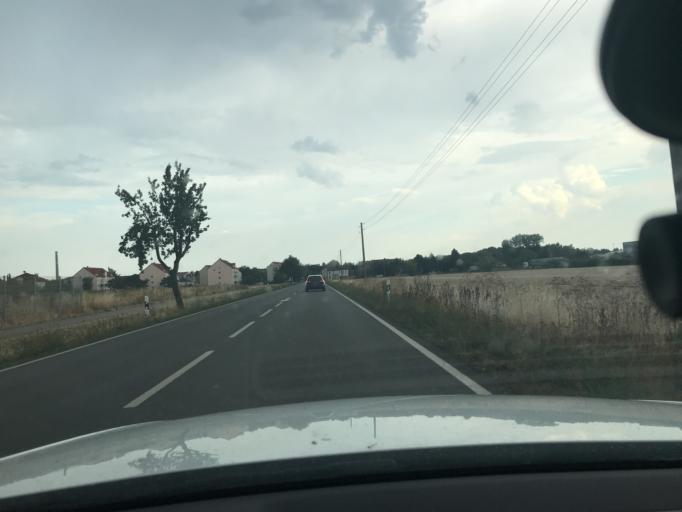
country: DE
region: Saxony
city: Markranstadt
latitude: 51.3101
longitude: 12.2145
